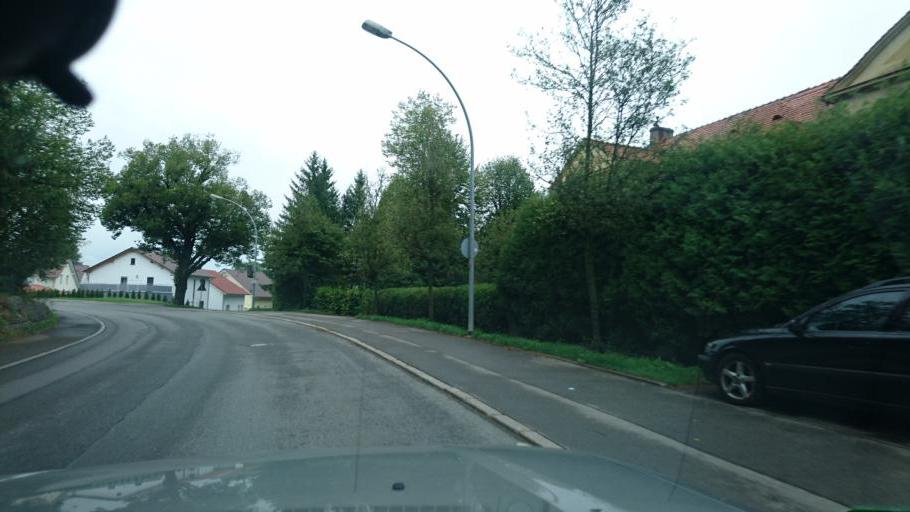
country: DE
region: Baden-Wuerttemberg
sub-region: Freiburg Region
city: Rottweil
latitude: 48.1729
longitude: 8.6177
